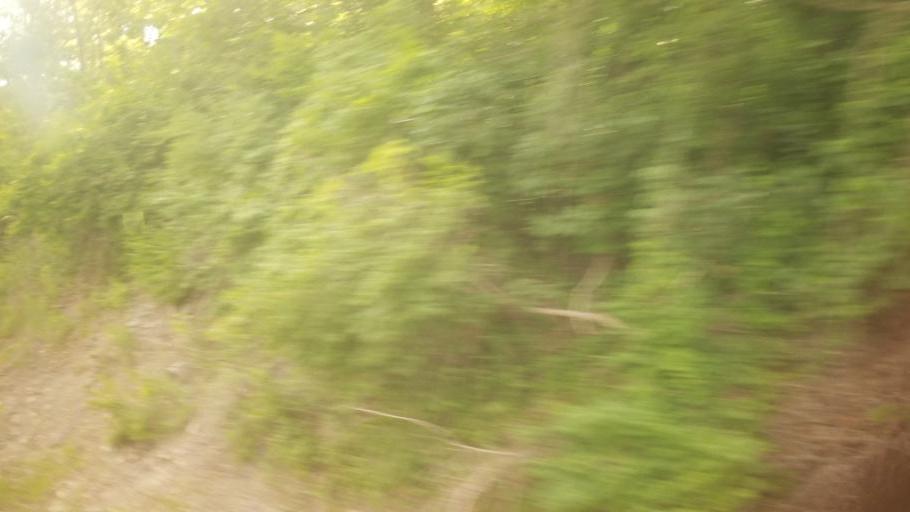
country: US
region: Missouri
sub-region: Jackson County
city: Sugar Creek
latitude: 39.1450
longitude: -94.4173
